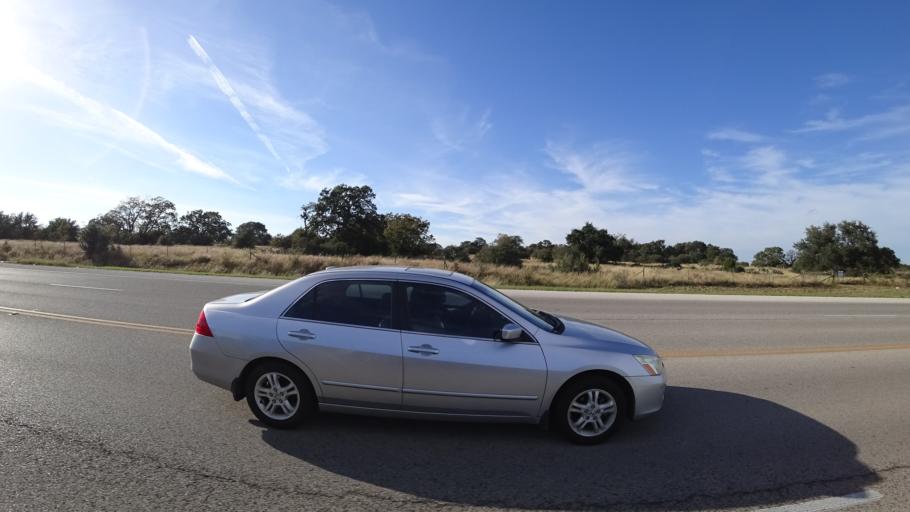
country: US
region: Texas
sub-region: Travis County
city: Wells Branch
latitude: 30.4515
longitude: -97.7256
